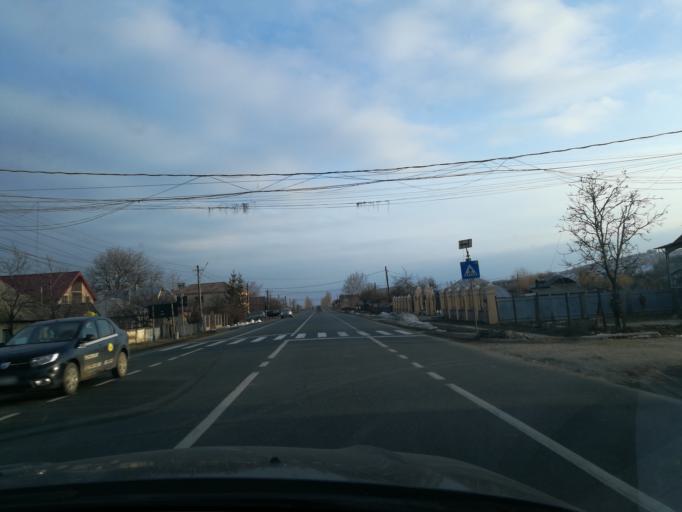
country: RO
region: Bacau
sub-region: Comuna Parava
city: Parava
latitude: 46.3232
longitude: 27.0144
